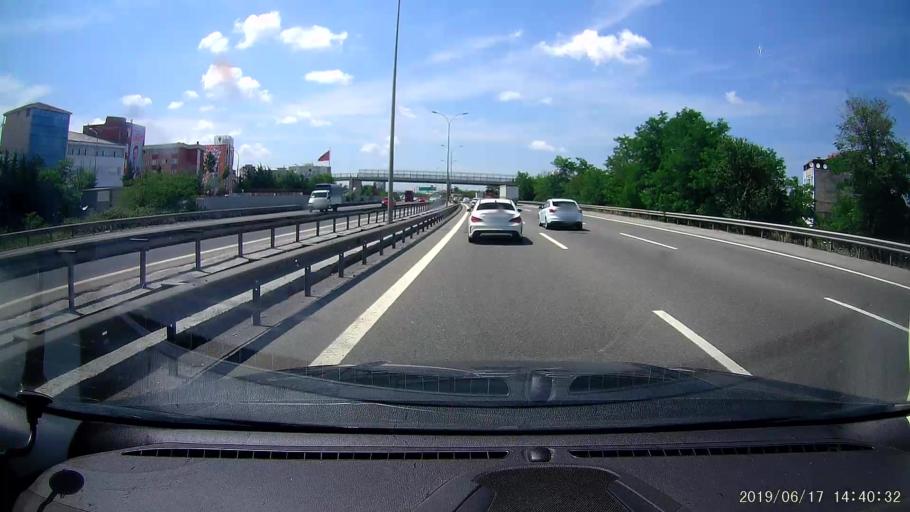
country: TR
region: Istanbul
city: Sultanbeyli
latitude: 40.9689
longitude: 29.2694
